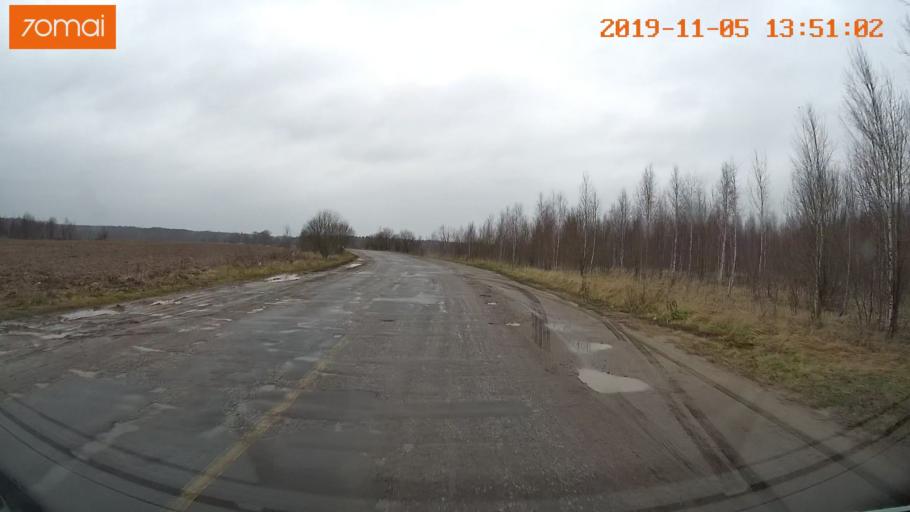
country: RU
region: Ivanovo
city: Kaminskiy
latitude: 57.0233
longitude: 41.4046
